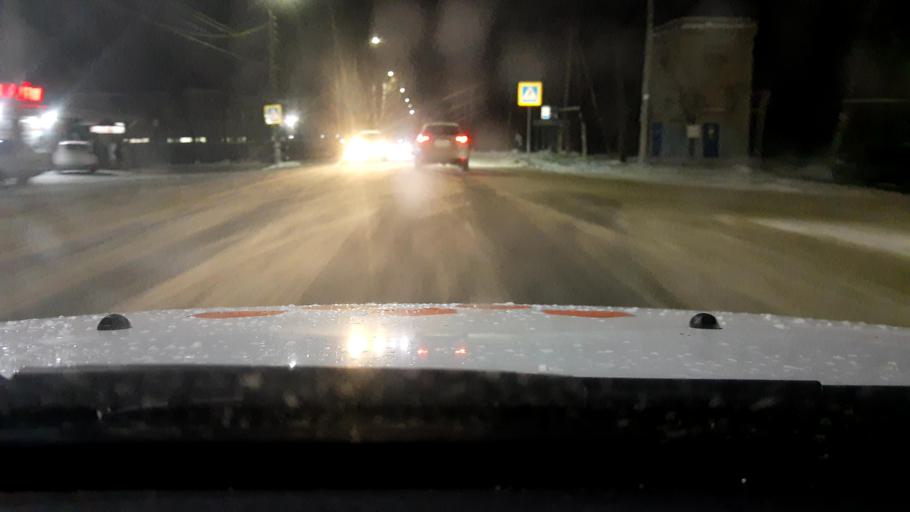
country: RU
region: Nizjnij Novgorod
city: Gorodets
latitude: 56.6563
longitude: 43.4867
